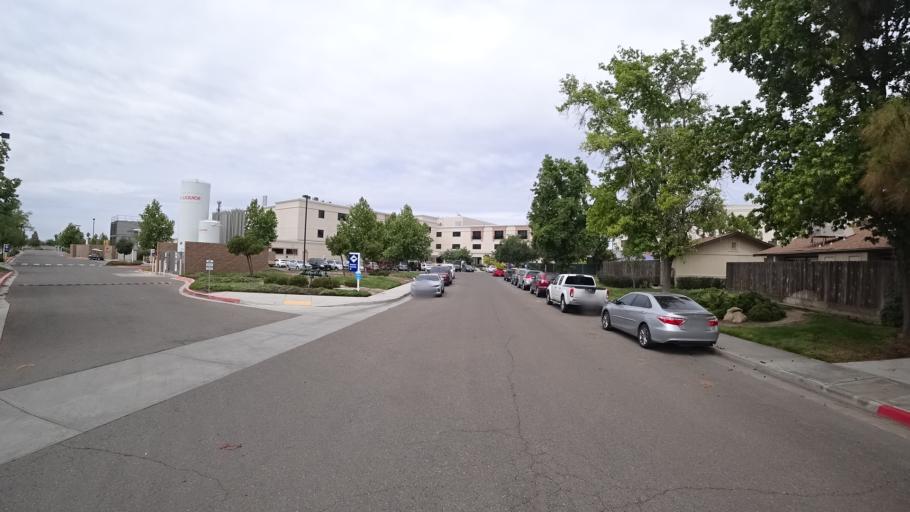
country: US
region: California
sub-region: Kings County
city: Hanford
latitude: 36.3239
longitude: -119.6657
